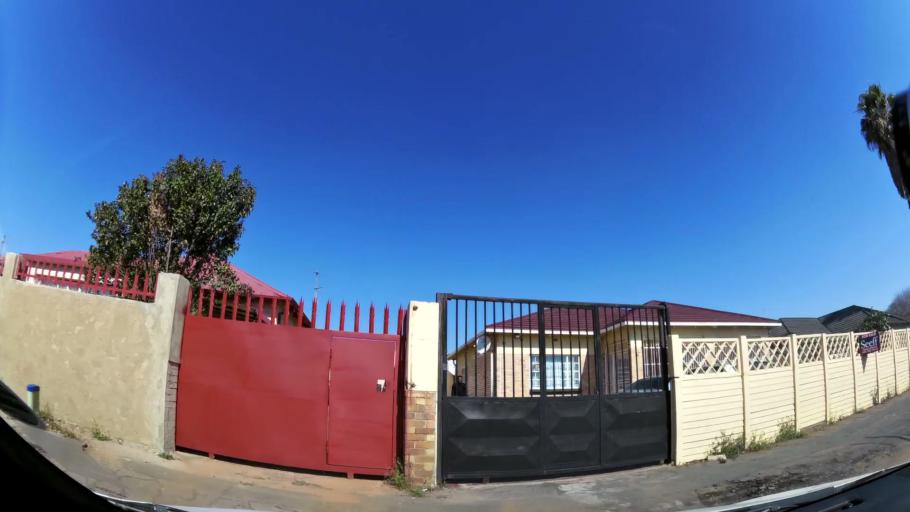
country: ZA
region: Gauteng
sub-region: City of Johannesburg Metropolitan Municipality
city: Johannesburg
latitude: -26.2402
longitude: 28.0745
